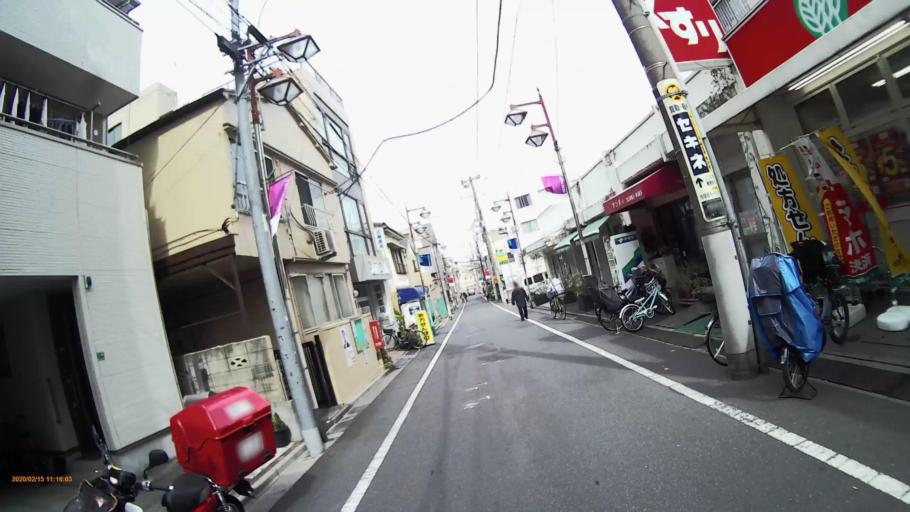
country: JP
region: Tokyo
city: Tokyo
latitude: 35.7431
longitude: 139.7137
